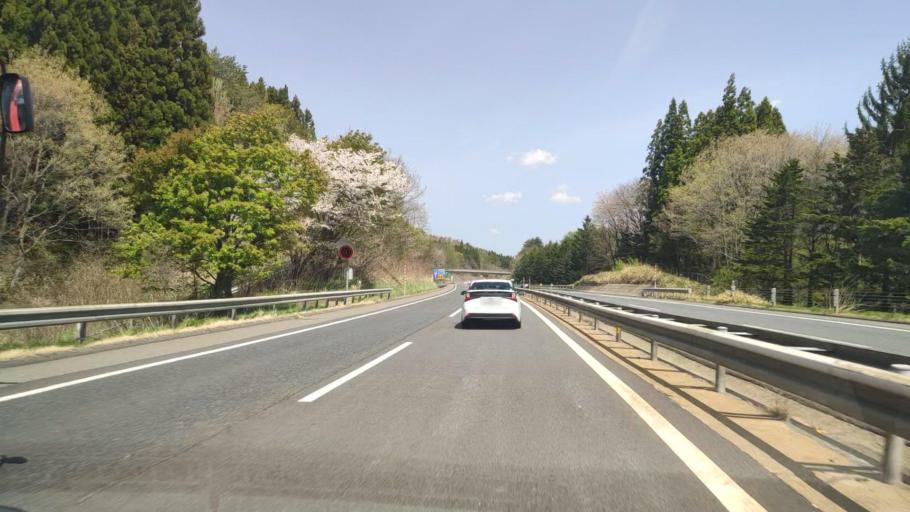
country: JP
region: Iwate
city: Ichinohe
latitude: 40.2427
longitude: 141.4010
